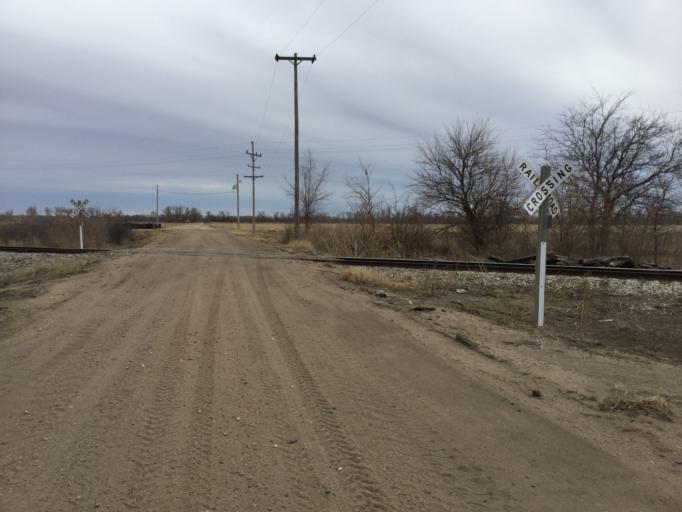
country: US
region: Kansas
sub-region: Reno County
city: Nickerson
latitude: 38.1749
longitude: -98.1245
